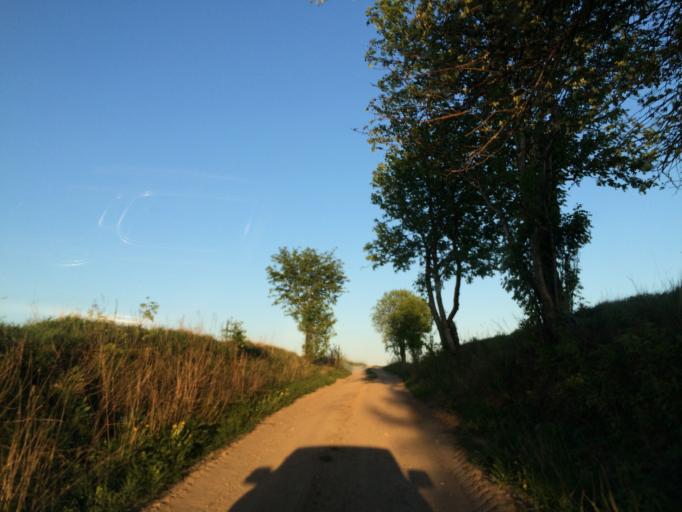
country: PL
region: Warmian-Masurian Voivodeship
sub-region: Powiat ilawski
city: Lubawa
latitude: 53.4896
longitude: 19.8520
